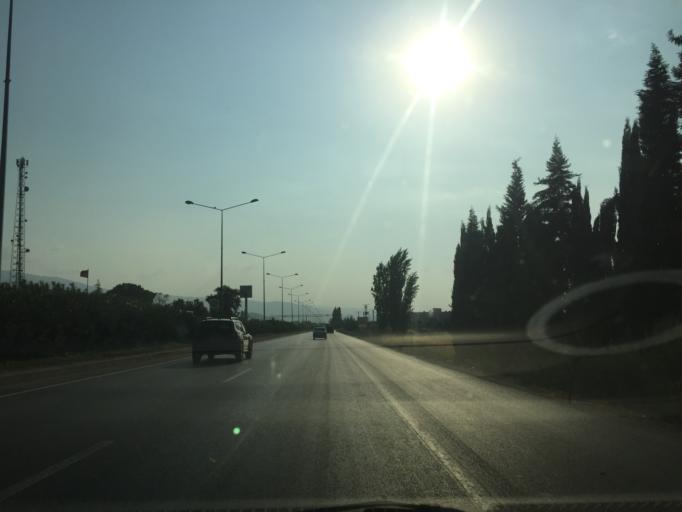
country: TR
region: Manisa
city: Salihli
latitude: 38.4946
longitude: 28.1790
